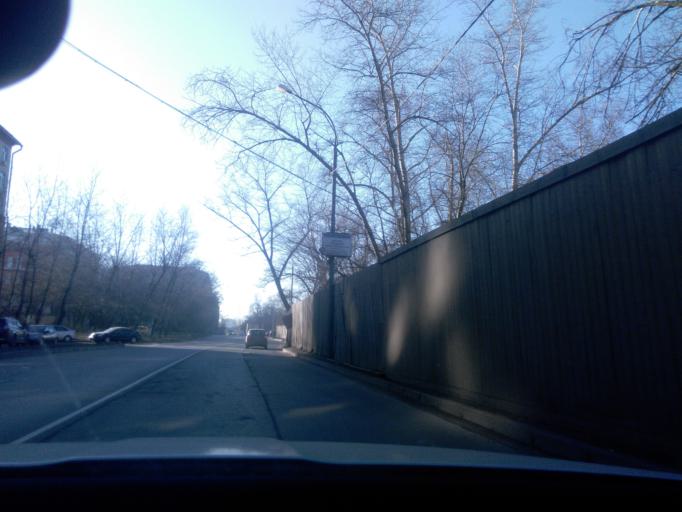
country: RU
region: Moscow
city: Sokol
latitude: 55.8036
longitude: 37.4959
